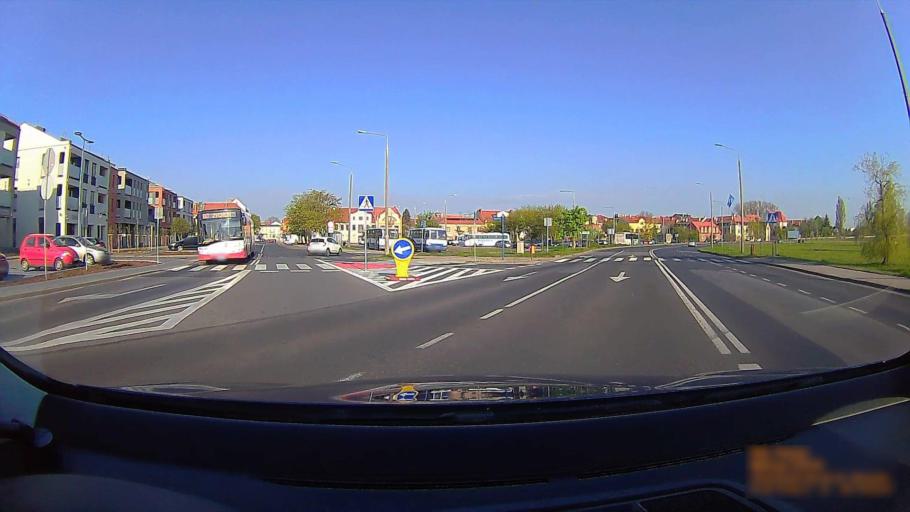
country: PL
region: Greater Poland Voivodeship
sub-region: Konin
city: Konin
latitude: 52.2095
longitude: 18.2594
